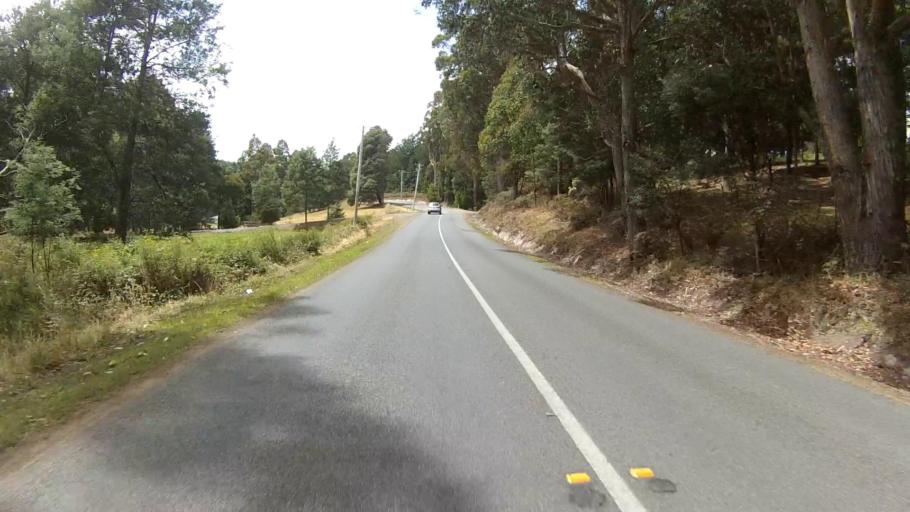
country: AU
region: Tasmania
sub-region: Kingborough
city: Kettering
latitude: -43.1069
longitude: 147.2332
